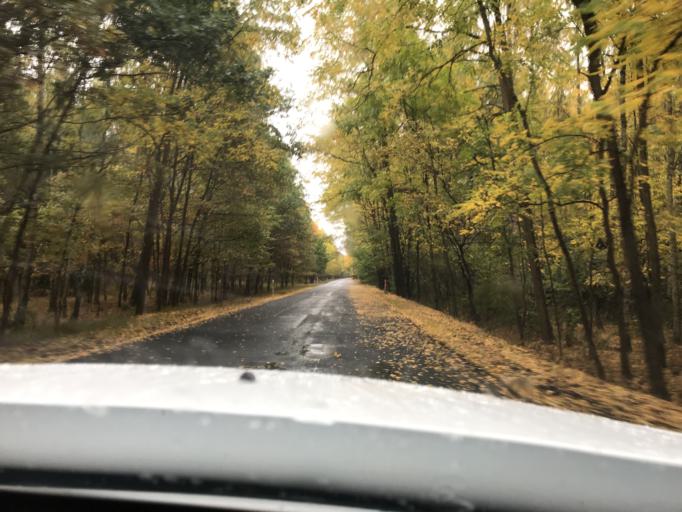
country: PL
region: West Pomeranian Voivodeship
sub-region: Powiat gryfinski
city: Mieszkowice
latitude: 52.7862
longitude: 14.4397
